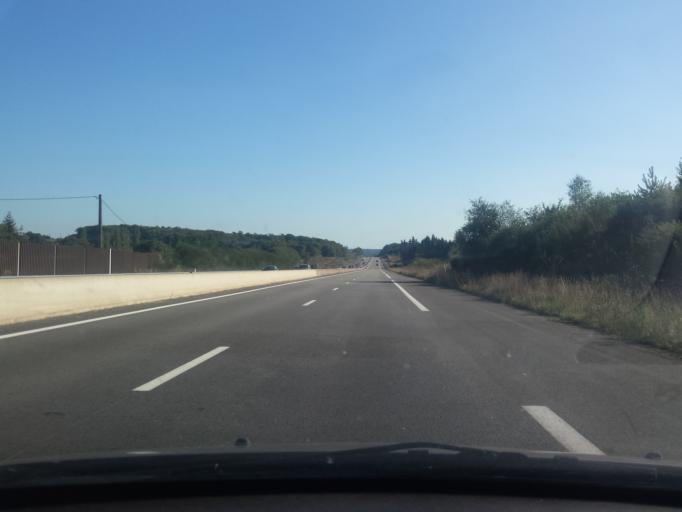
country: FR
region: Brittany
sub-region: Departement du Morbihan
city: Colpo
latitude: 47.8053
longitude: -2.8076
